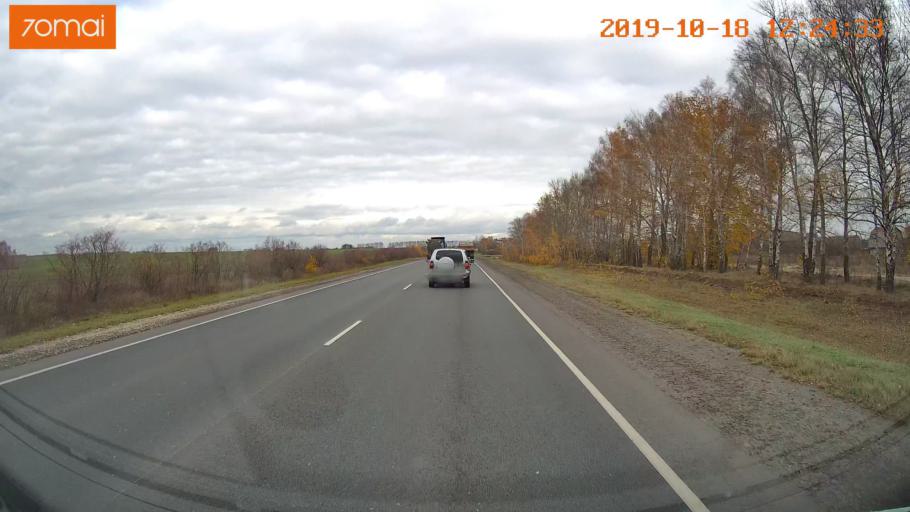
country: RU
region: Rjazan
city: Rybnoye
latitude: 54.5401
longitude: 39.5139
